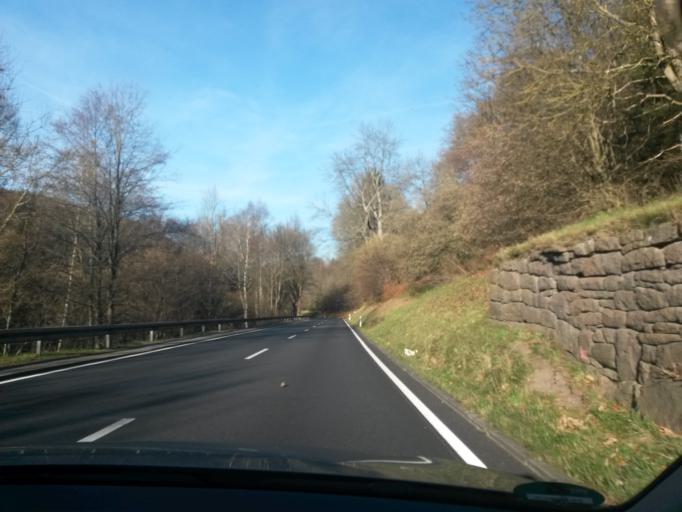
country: DE
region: Baden-Wuerttemberg
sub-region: Karlsruhe Region
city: Hofen an der Enz
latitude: 48.7856
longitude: 8.5798
